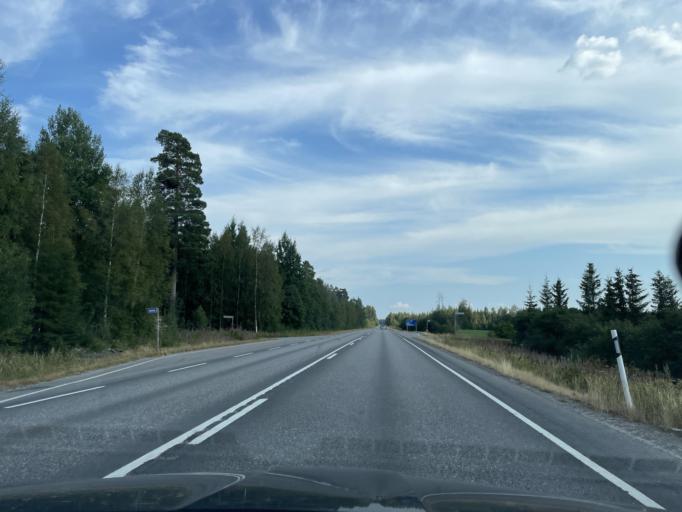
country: FI
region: Central Finland
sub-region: Jaemsae
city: Kuhmoinen
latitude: 61.6655
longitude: 25.2744
